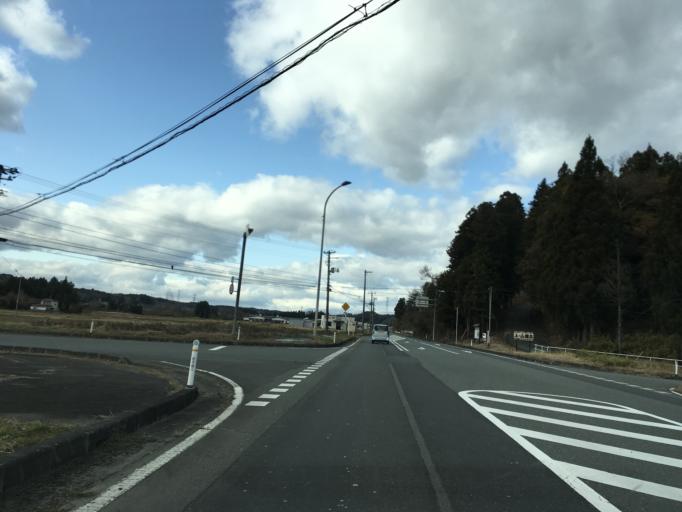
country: JP
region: Iwate
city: Ichinoseki
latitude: 38.8548
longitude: 141.1698
